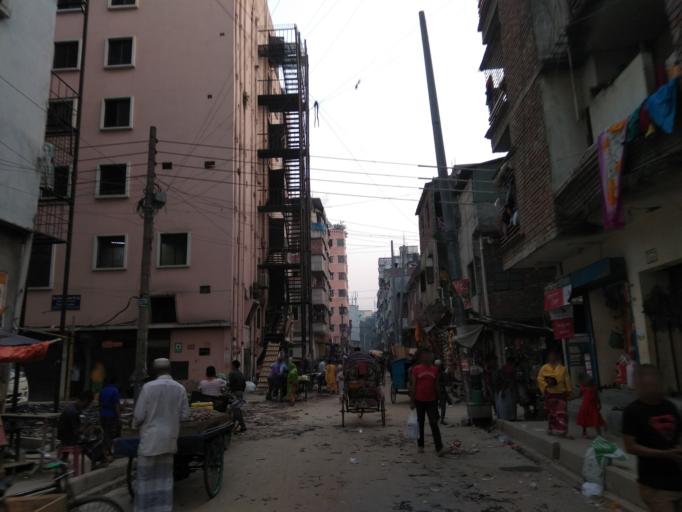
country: BD
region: Dhaka
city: Tungi
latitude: 23.8174
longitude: 90.3639
